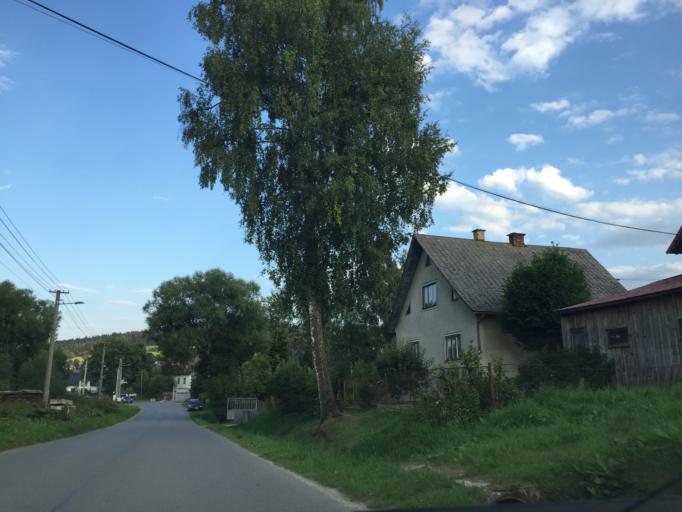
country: PL
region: Silesian Voivodeship
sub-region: Powiat zywiecki
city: Korbielow
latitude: 49.4611
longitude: 19.3374
